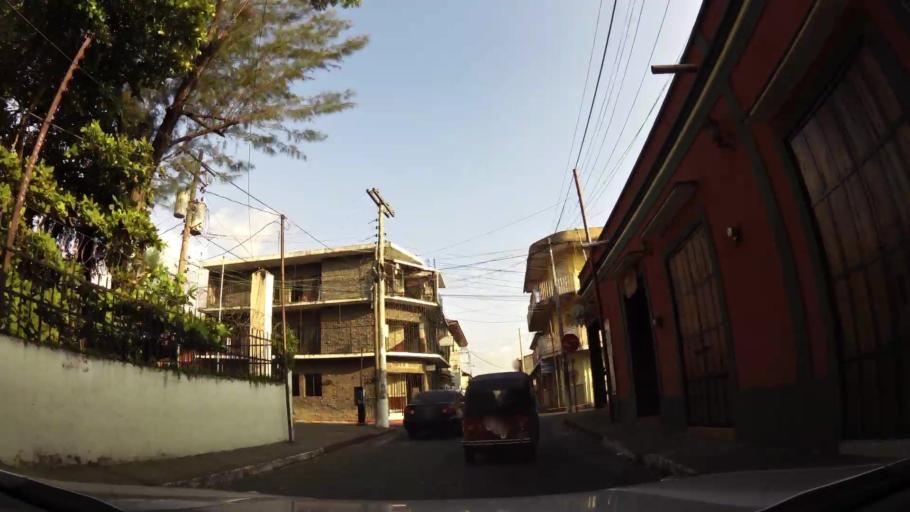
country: GT
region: Retalhuleu
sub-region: Municipio de Retalhuleu
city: Retalhuleu
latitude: 14.5350
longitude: -91.6777
